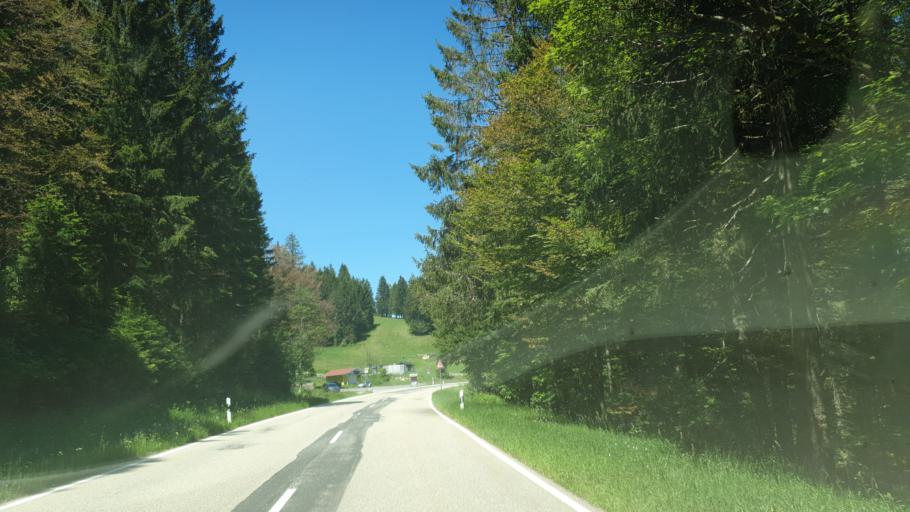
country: DE
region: Baden-Wuerttemberg
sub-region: Freiburg Region
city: Wieden
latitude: 47.8833
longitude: 7.8981
